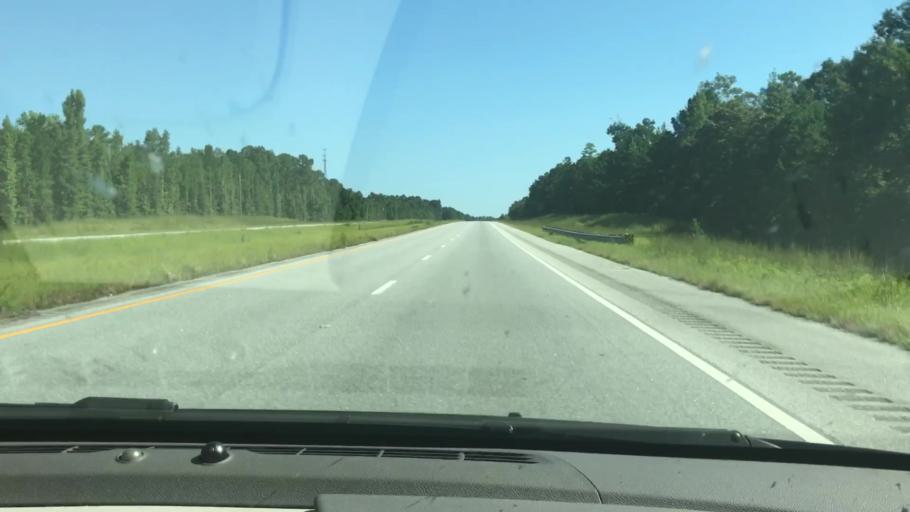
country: US
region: Alabama
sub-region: Russell County
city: Ladonia
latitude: 32.3818
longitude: -85.0830
